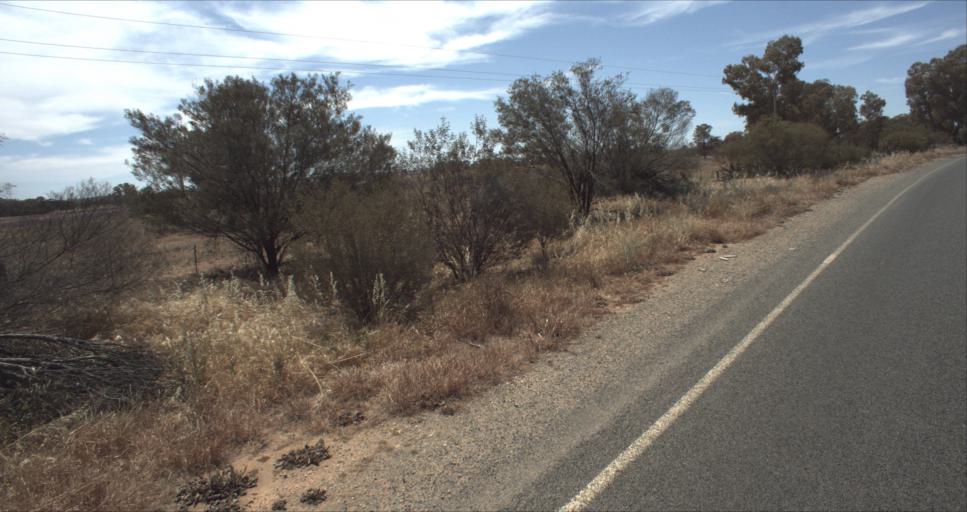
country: AU
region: New South Wales
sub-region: Leeton
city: Leeton
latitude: -34.6604
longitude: 146.4530
